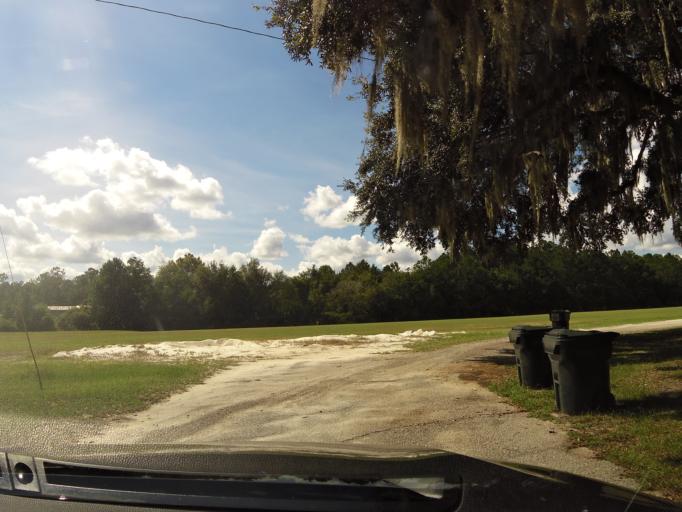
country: US
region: Georgia
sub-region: Clinch County
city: Homerville
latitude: 30.6903
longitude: -82.5662
